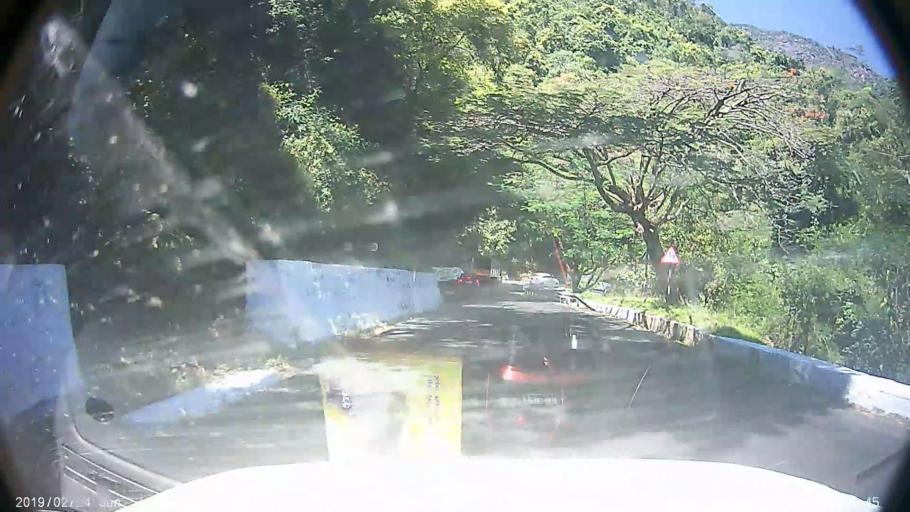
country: IN
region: Tamil Nadu
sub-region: Nilgiri
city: Wellington
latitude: 11.3410
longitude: 76.8452
